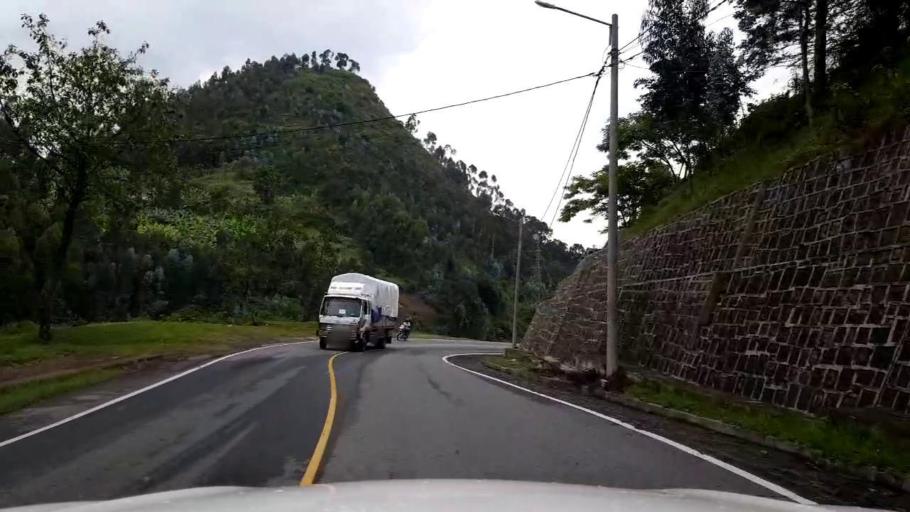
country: RW
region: Western Province
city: Gisenyi
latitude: -1.7034
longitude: 29.2704
